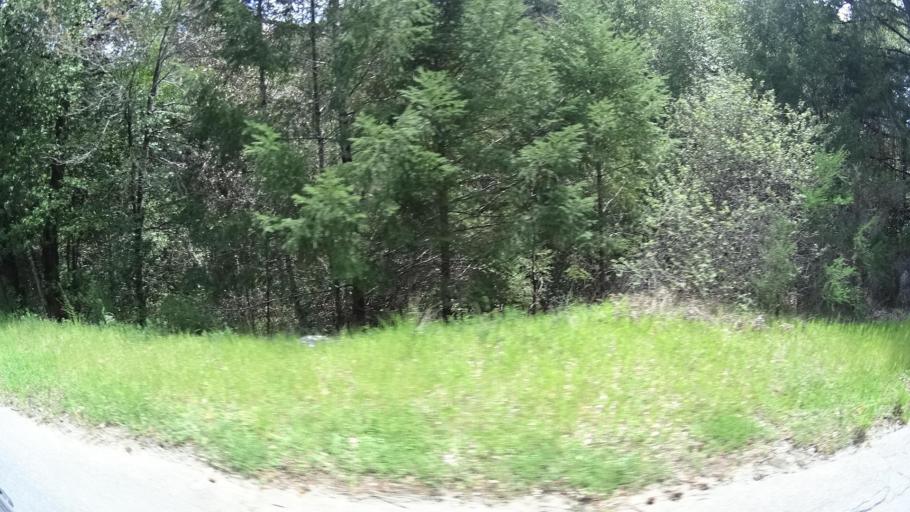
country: US
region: California
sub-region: Humboldt County
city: Redway
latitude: 40.0677
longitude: -123.9612
